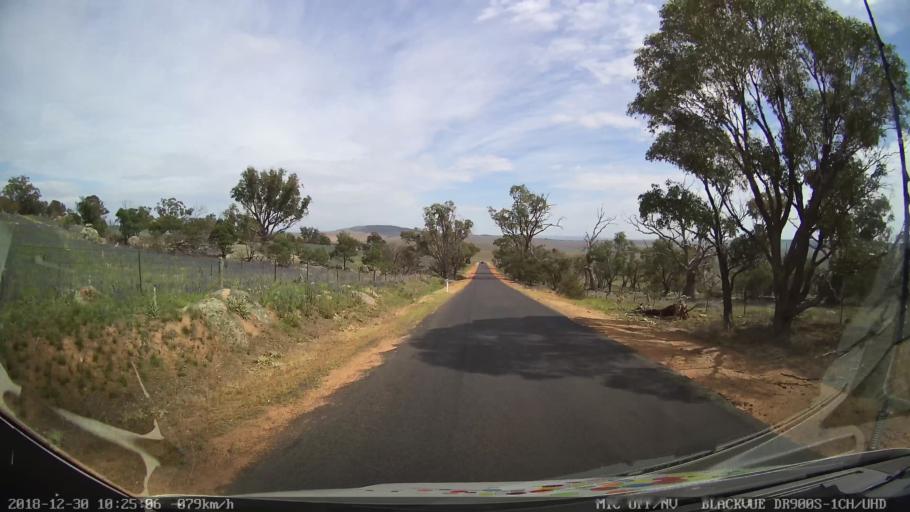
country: AU
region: New South Wales
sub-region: Snowy River
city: Berridale
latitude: -36.5285
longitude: 148.9615
